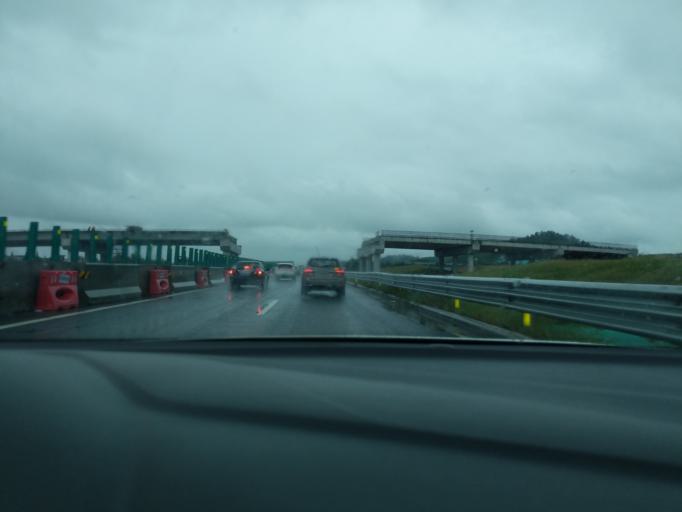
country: CN
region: Guangdong
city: Yueshan
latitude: 22.4640
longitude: 112.7095
